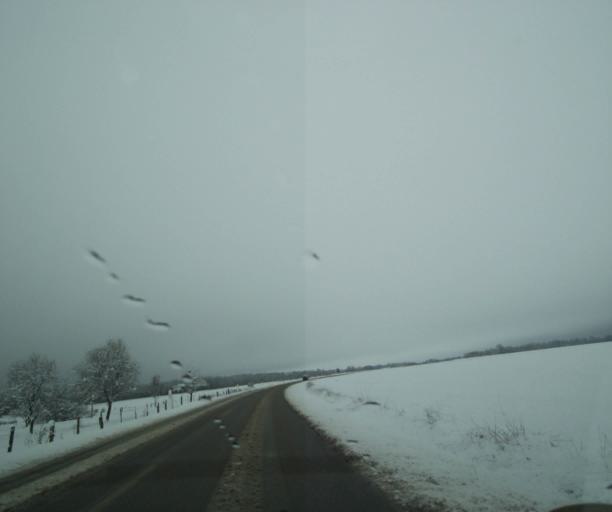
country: FR
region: Champagne-Ardenne
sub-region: Departement de la Haute-Marne
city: Wassy
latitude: 48.5316
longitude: 4.9257
